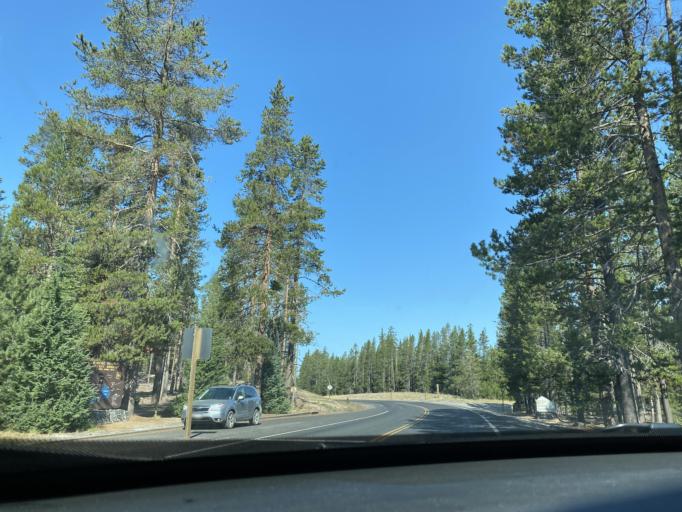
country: US
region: Oregon
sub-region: Deschutes County
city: Three Rivers
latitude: 43.7118
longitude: -121.2767
